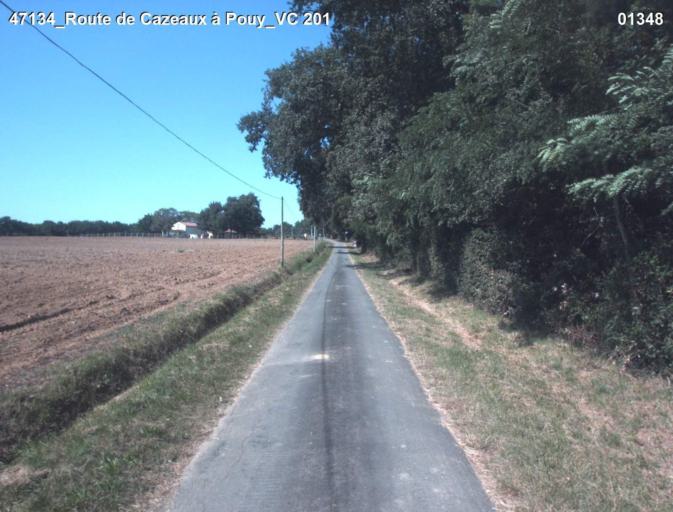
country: FR
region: Aquitaine
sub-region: Departement du Lot-et-Garonne
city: Mezin
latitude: 44.0159
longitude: 0.3069
